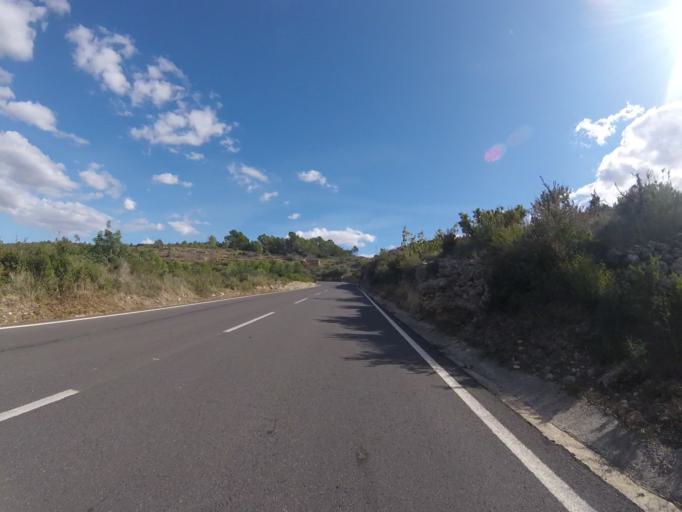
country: ES
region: Valencia
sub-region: Provincia de Castello
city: Cuevas de Vinroma
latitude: 40.3146
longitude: 0.1347
